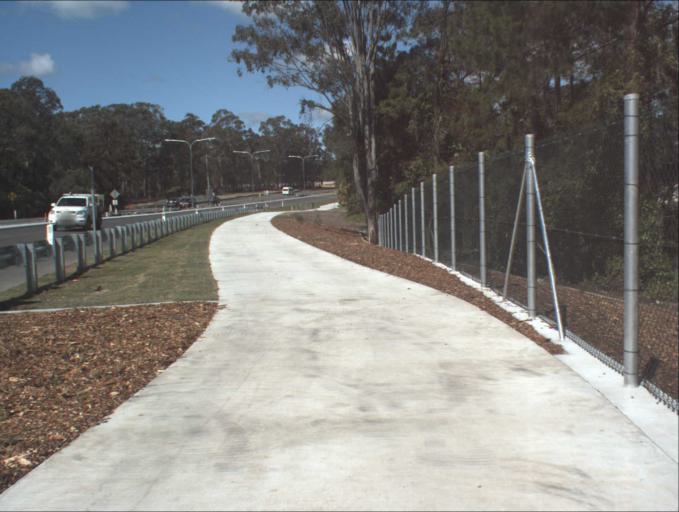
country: AU
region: Queensland
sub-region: Logan
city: Waterford West
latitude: -27.6942
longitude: 153.1023
